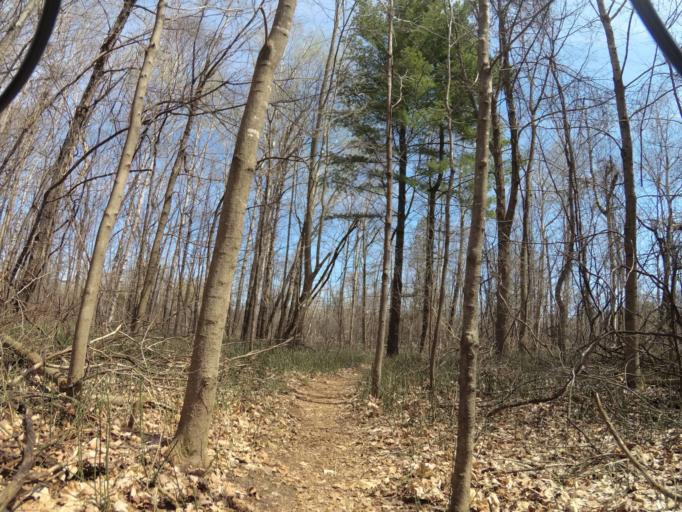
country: CA
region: Ontario
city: Ottawa
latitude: 45.3545
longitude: -75.6758
